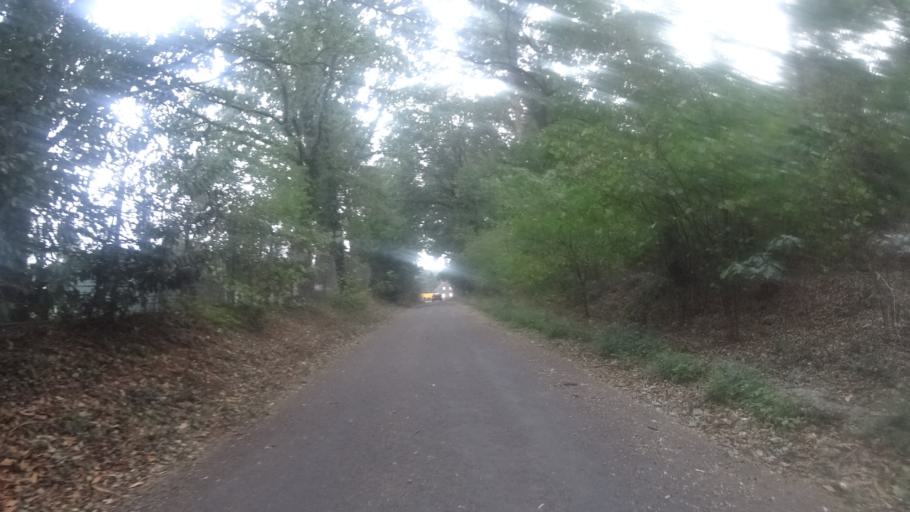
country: NL
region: Limburg
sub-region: Gemeente Venlo
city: Arcen
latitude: 51.4783
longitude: 6.2156
